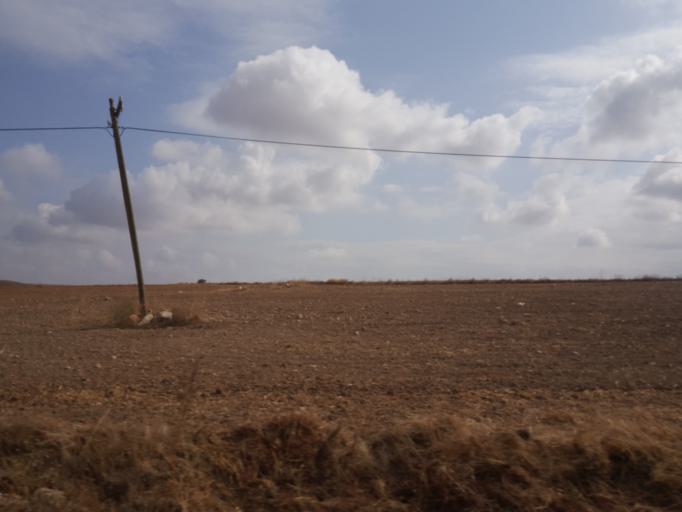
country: TR
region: Kirikkale
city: Keskin
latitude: 39.6065
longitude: 33.6134
